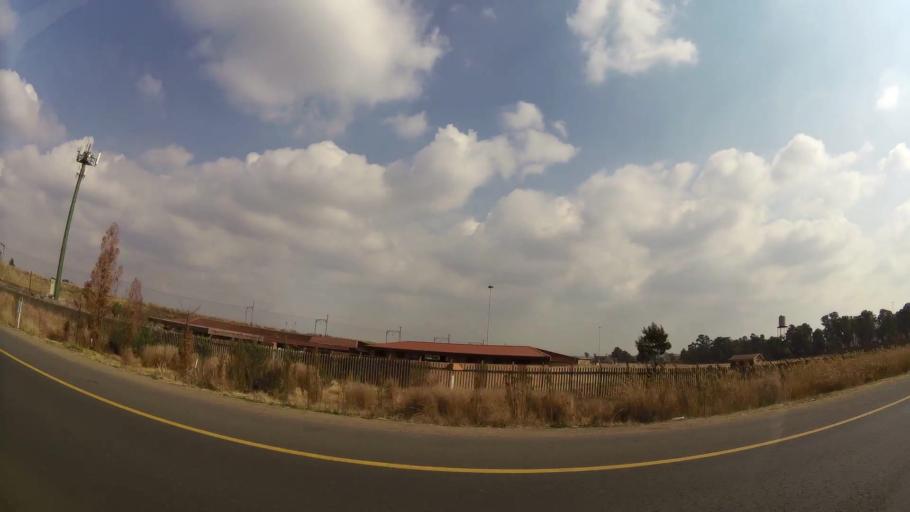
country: ZA
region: Gauteng
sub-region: Ekurhuleni Metropolitan Municipality
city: Brakpan
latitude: -26.1694
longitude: 28.3974
